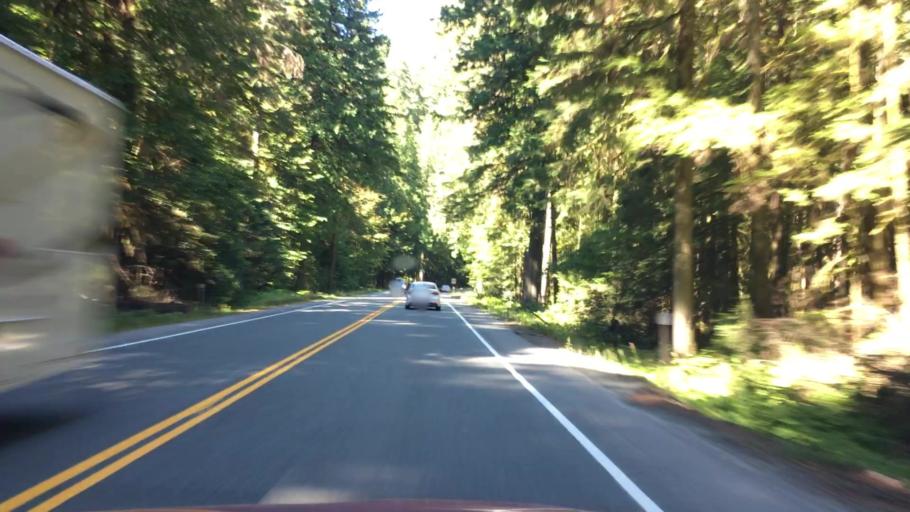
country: CA
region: British Columbia
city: Port Alberni
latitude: 49.2797
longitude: -124.6752
